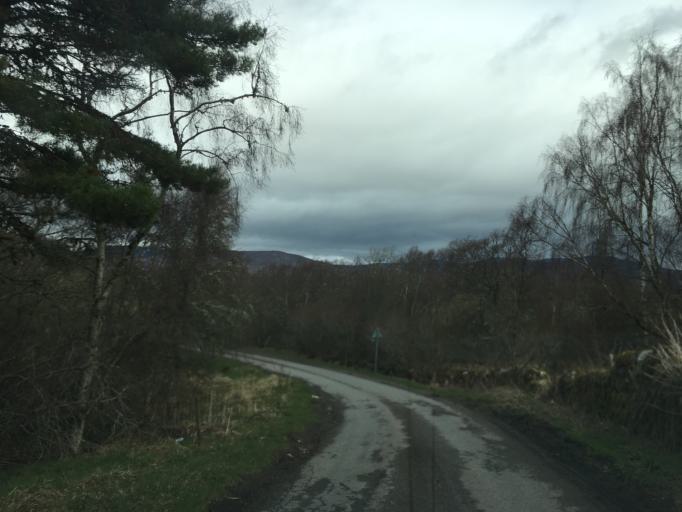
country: GB
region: Scotland
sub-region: Highland
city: Aviemore
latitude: 57.1096
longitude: -3.9217
